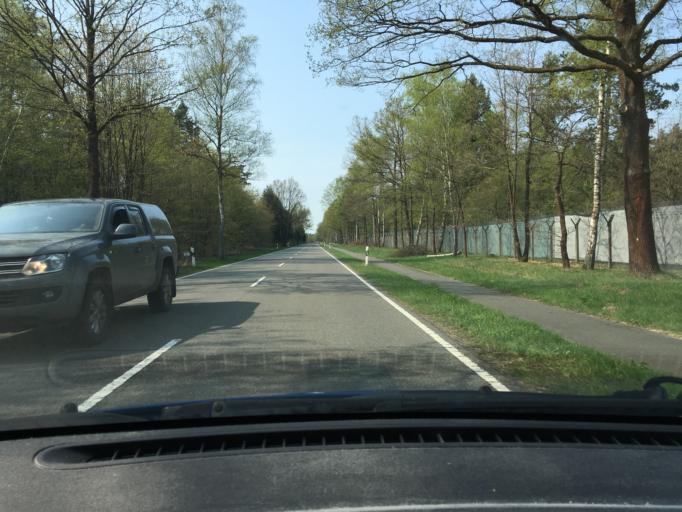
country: DE
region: Lower Saxony
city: Unterluss
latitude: 52.8571
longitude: 10.2781
